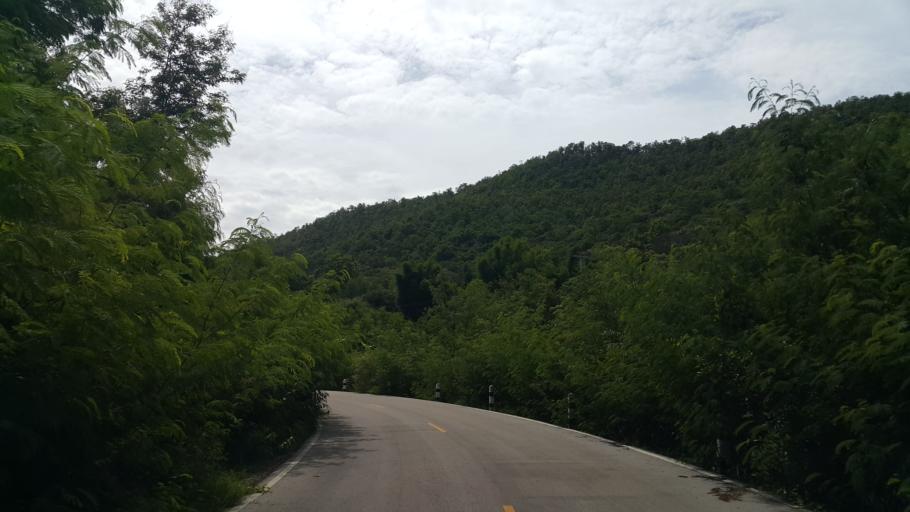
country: TH
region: Chiang Mai
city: Mae On
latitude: 18.7462
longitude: 99.1997
